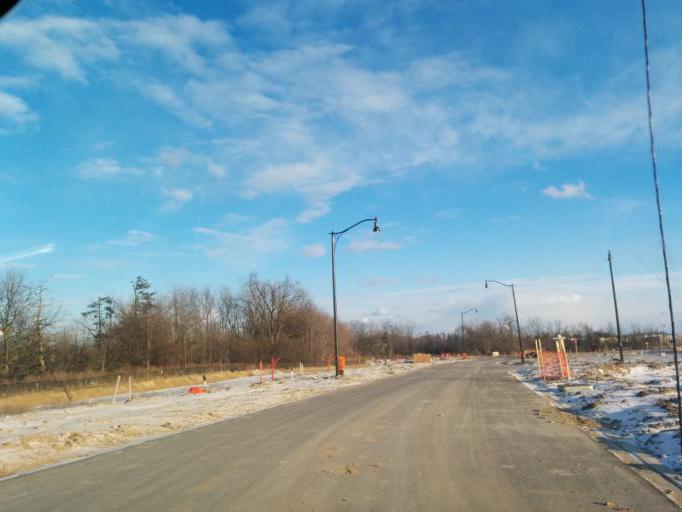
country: CA
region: Ontario
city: Brampton
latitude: 43.6635
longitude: -79.8190
